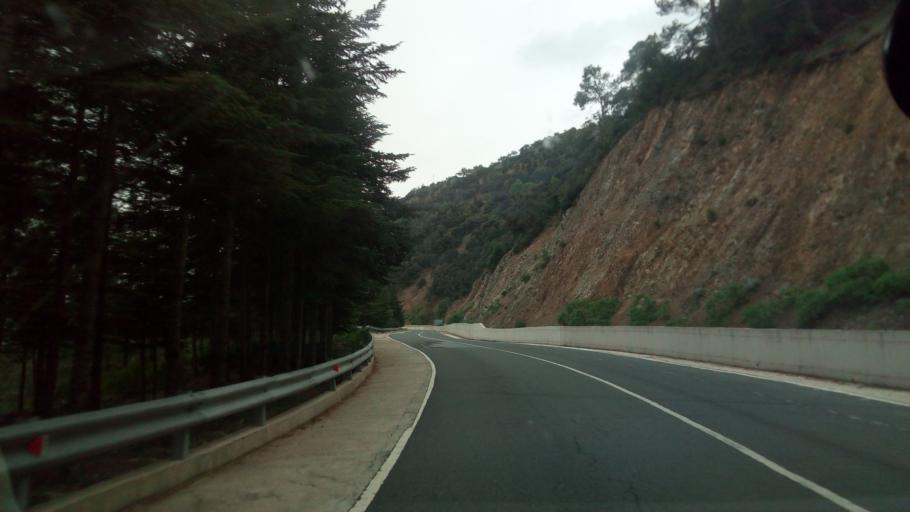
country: CY
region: Lefkosia
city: Lefka
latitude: 34.9897
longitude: 32.7385
